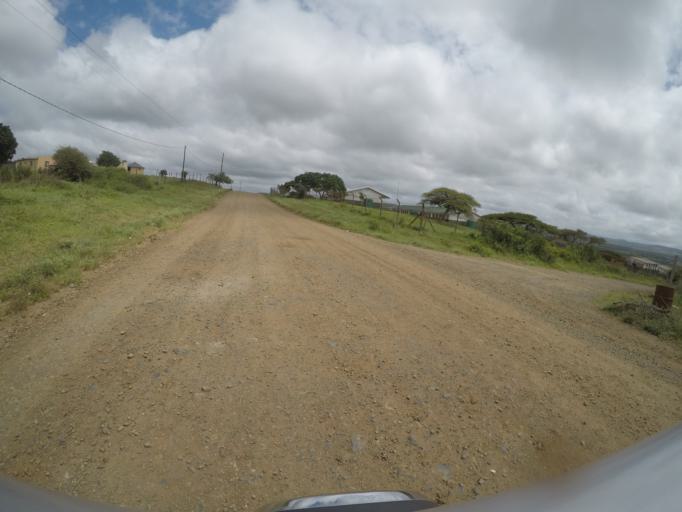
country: ZA
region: KwaZulu-Natal
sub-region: uThungulu District Municipality
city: Empangeni
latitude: -28.5771
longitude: 31.8436
